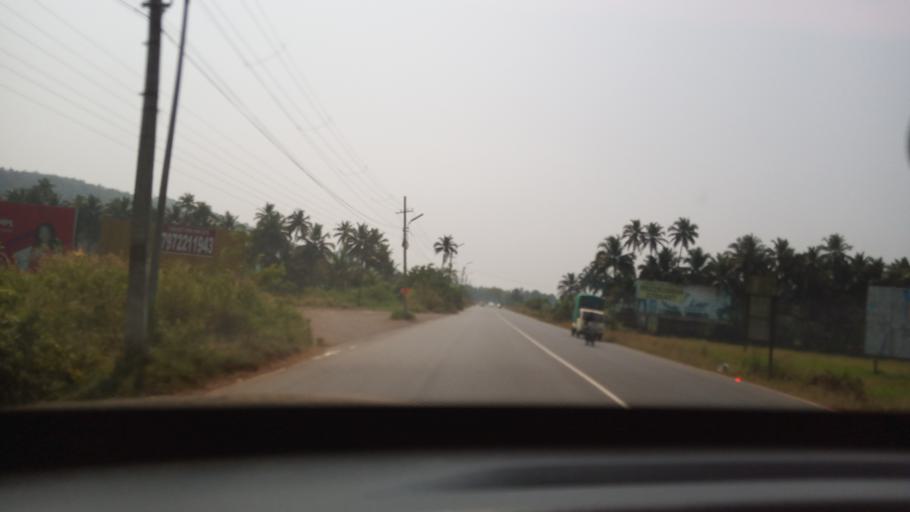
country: IN
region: Goa
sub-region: South Goa
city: Sancoale
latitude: 15.3450
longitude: 73.9273
